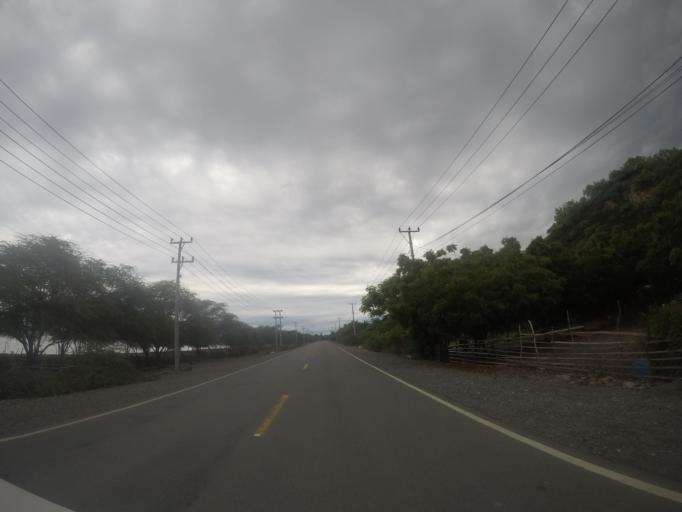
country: TL
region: Liquica
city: Liquica
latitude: -8.5667
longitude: 125.3885
